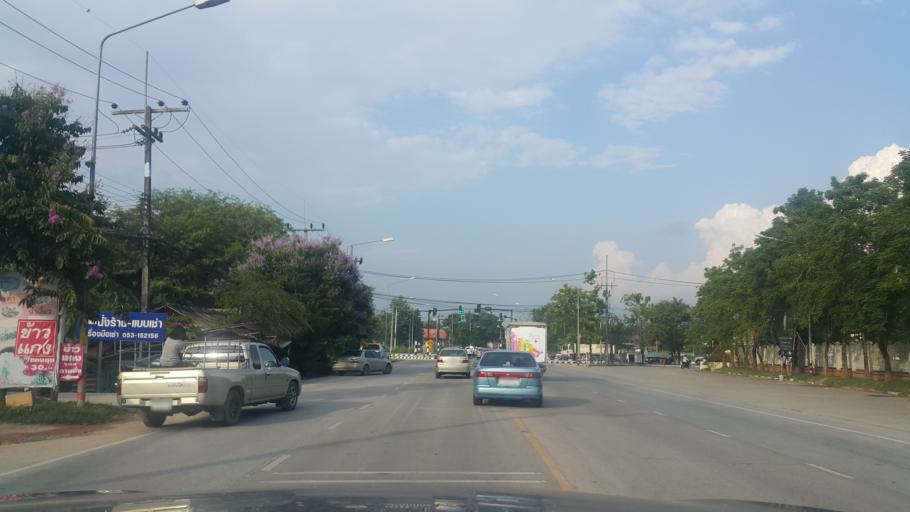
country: TH
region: Chiang Rai
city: Chiang Rai
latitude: 19.9302
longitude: 99.8626
